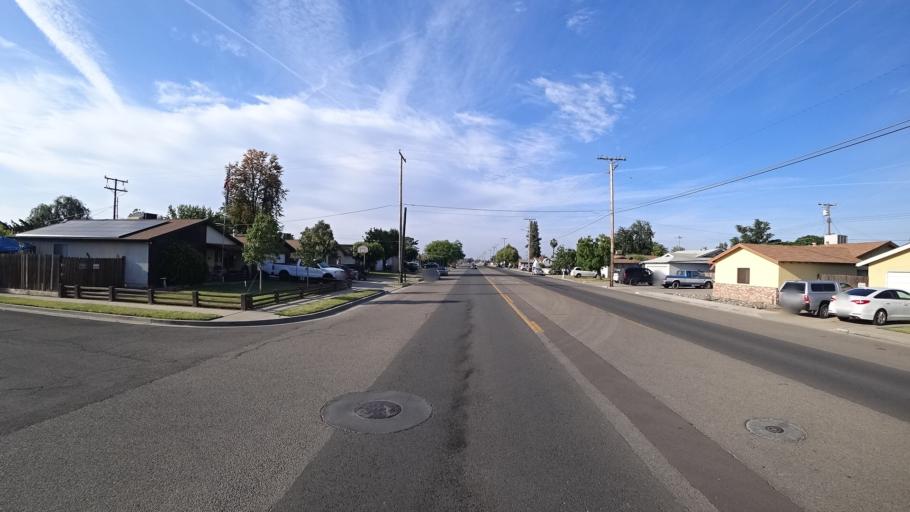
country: US
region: California
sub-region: Kings County
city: Hanford
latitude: 36.3114
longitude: -119.6729
